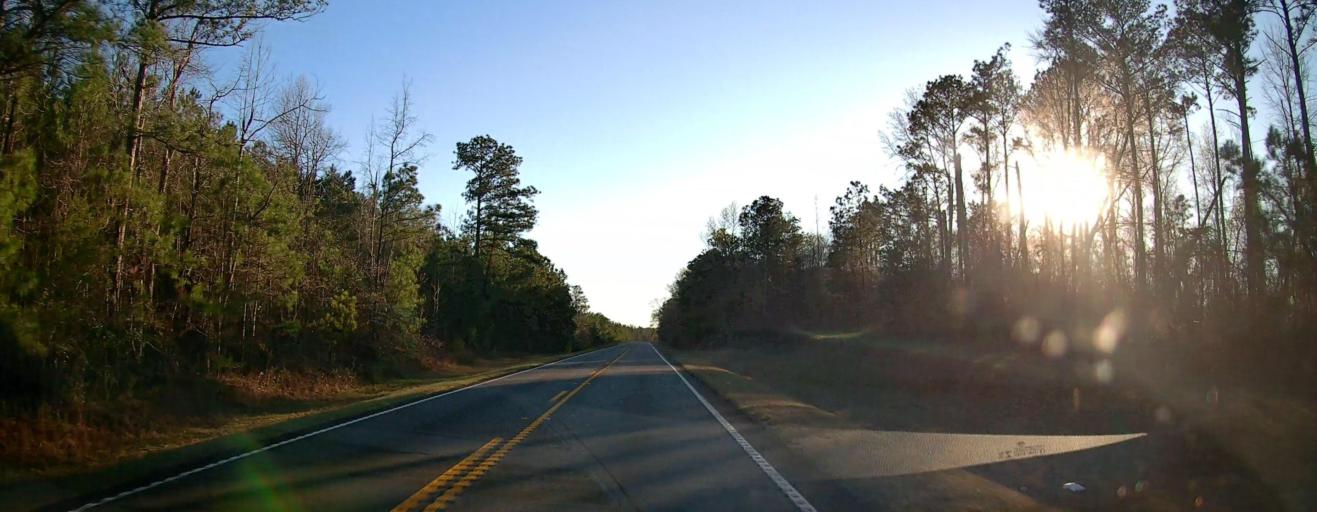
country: US
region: Georgia
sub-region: Talbot County
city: Talbotton
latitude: 32.6528
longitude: -84.6714
